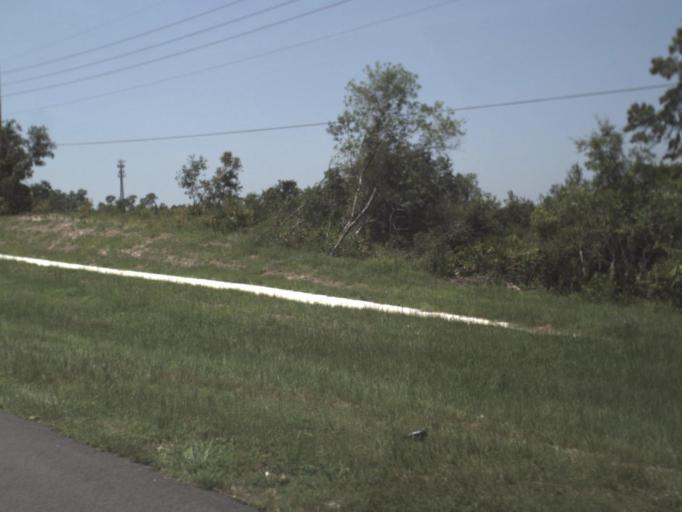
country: US
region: Florida
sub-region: Hernando County
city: North Weeki Wachee
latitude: 28.5290
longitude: -82.5686
